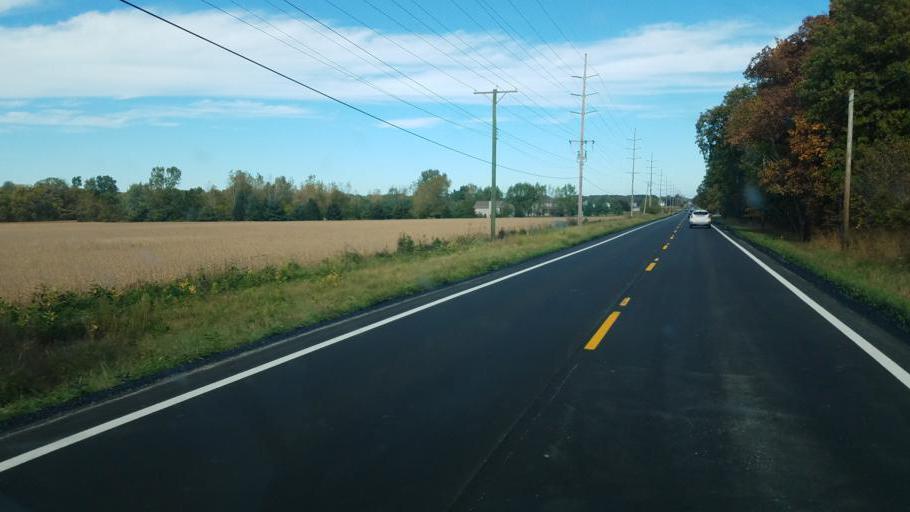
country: US
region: Ohio
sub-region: Erie County
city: Huron
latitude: 41.3384
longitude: -82.4937
